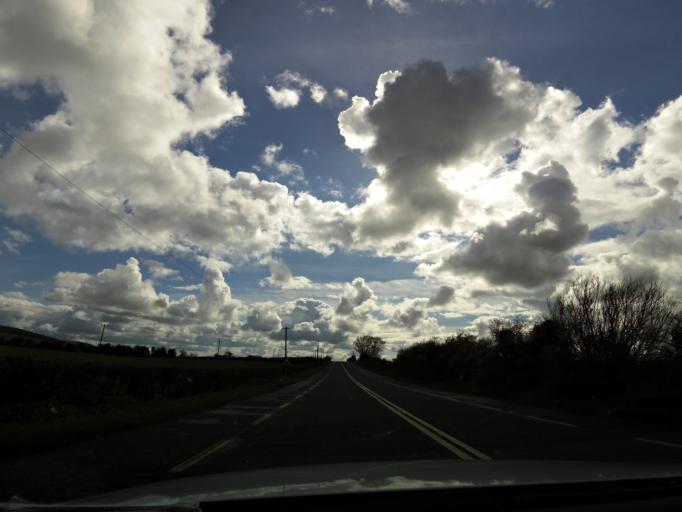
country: IE
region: Leinster
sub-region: Laois
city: Rathdowney
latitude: 52.8039
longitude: -7.4998
